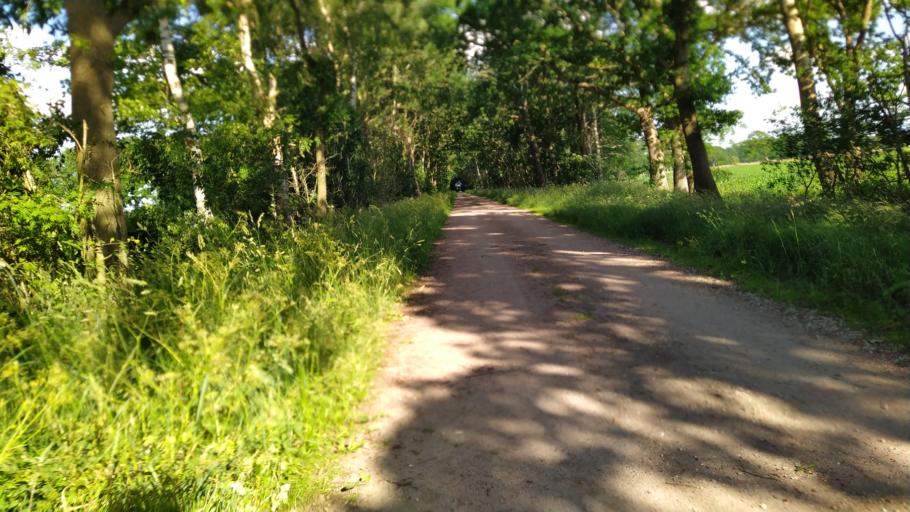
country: DE
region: Lower Saxony
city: Lintig
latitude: 53.6167
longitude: 8.8813
